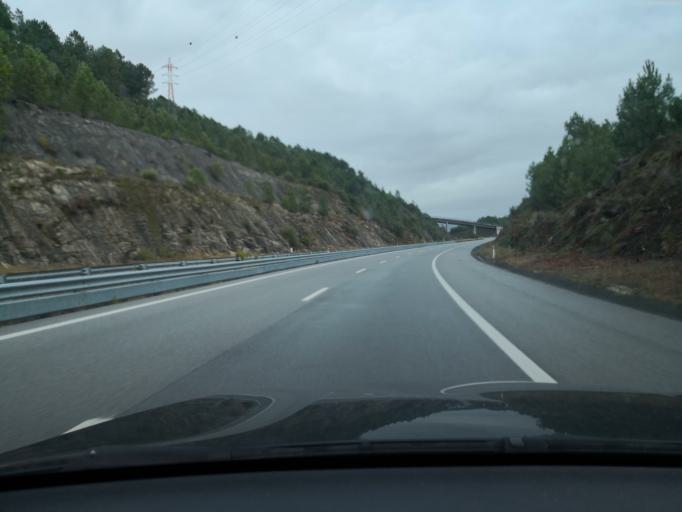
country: PT
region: Vila Real
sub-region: Ribeira de Pena
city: Ribeira de Pena
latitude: 41.4774
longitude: -7.8819
